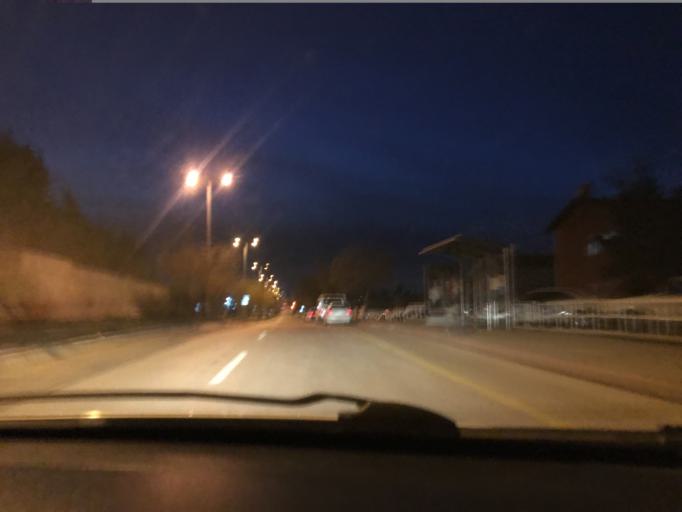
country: TR
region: Ankara
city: Batikent
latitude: 39.9601
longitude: 32.7423
